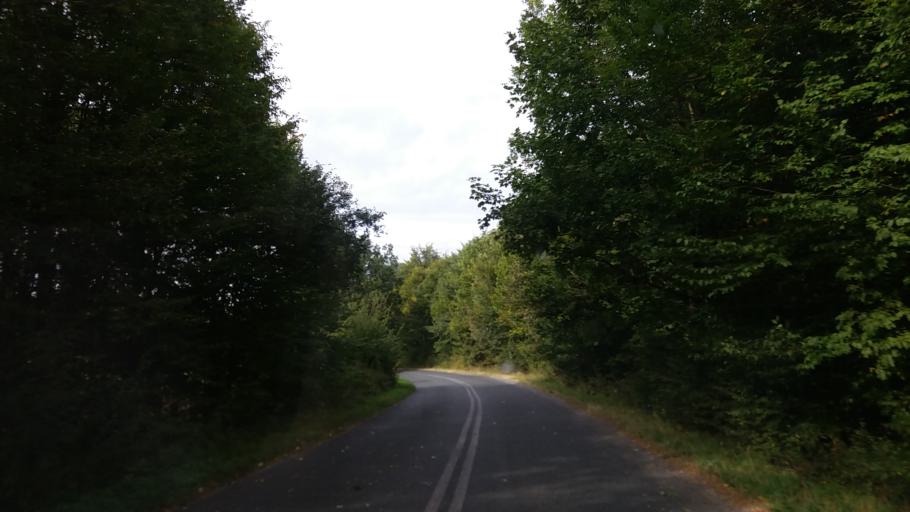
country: PL
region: West Pomeranian Voivodeship
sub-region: Powiat choszczenski
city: Krzecin
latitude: 53.0229
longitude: 15.5115
